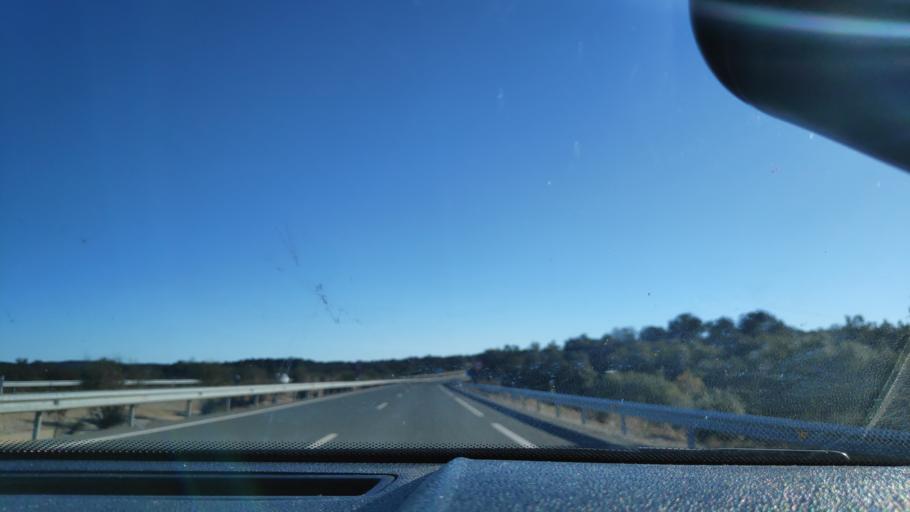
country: ES
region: Andalusia
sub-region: Provincia de Huelva
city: Santa Olalla del Cala
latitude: 37.9426
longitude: -6.2277
